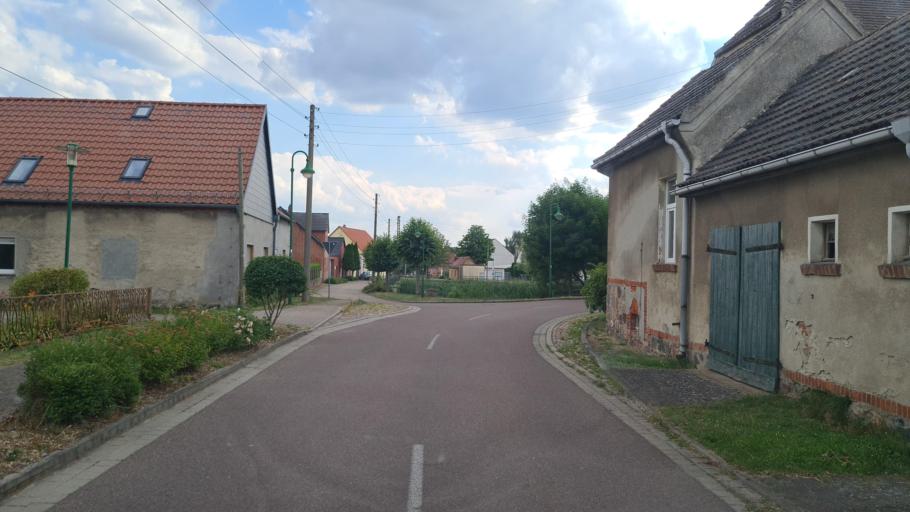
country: DE
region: Saxony-Anhalt
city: Kropstadt
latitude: 51.9758
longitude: 12.6826
